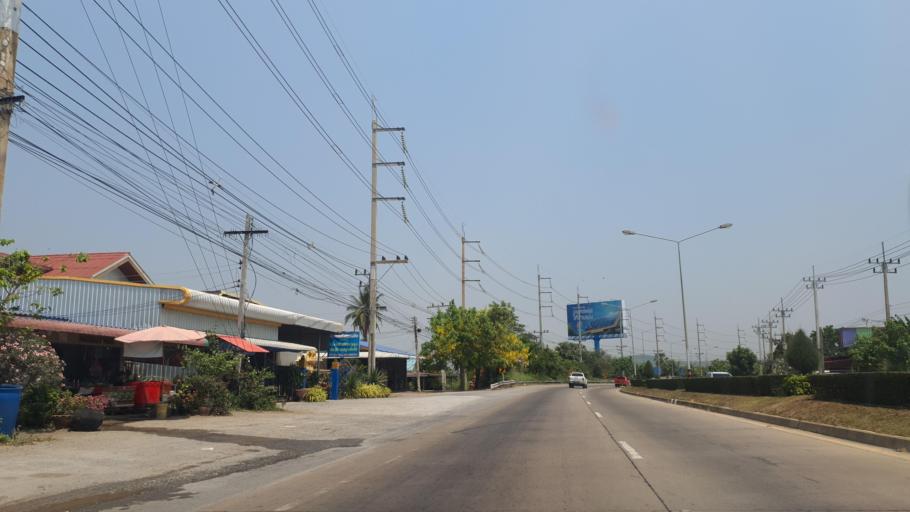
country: TH
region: Suphan Buri
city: U Thong
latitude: 14.3243
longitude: 99.8618
